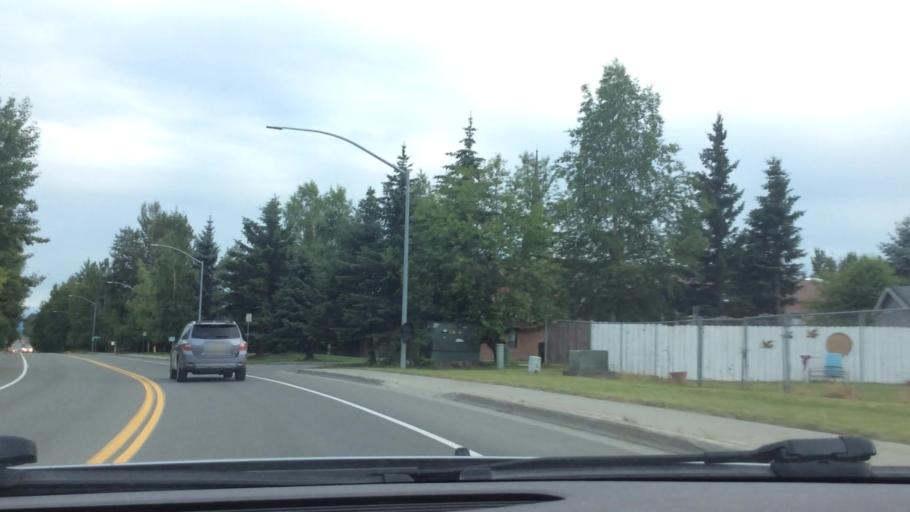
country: US
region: Alaska
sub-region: Anchorage Municipality
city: Anchorage
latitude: 61.2009
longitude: -149.7634
